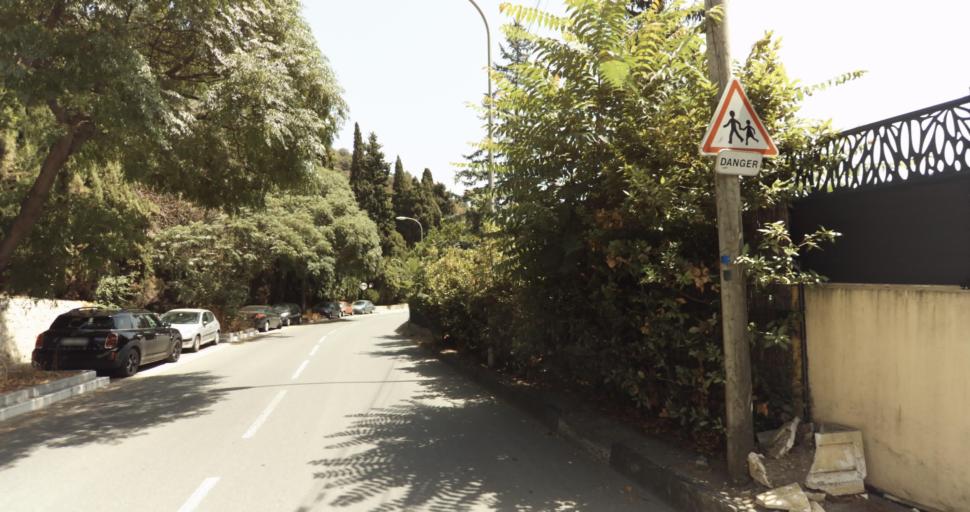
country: FR
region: Provence-Alpes-Cote d'Azur
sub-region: Departement des Alpes-Maritimes
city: Roquebrune-Cap-Martin
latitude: 43.7751
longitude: 7.4743
